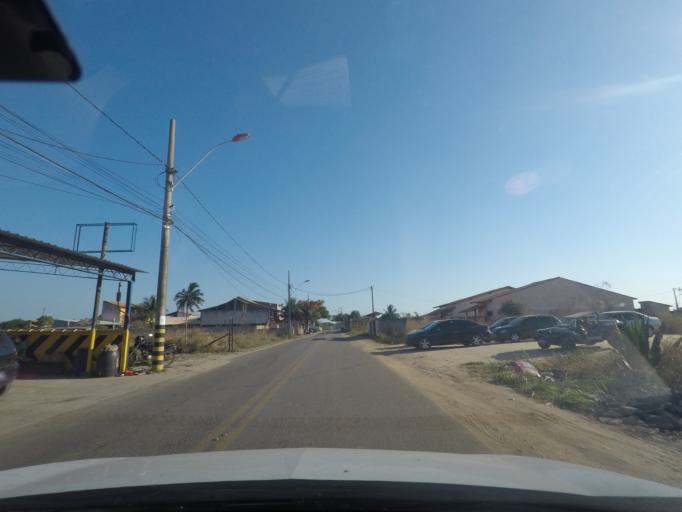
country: BR
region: Rio de Janeiro
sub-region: Marica
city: Marica
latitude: -22.9576
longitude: -42.9425
